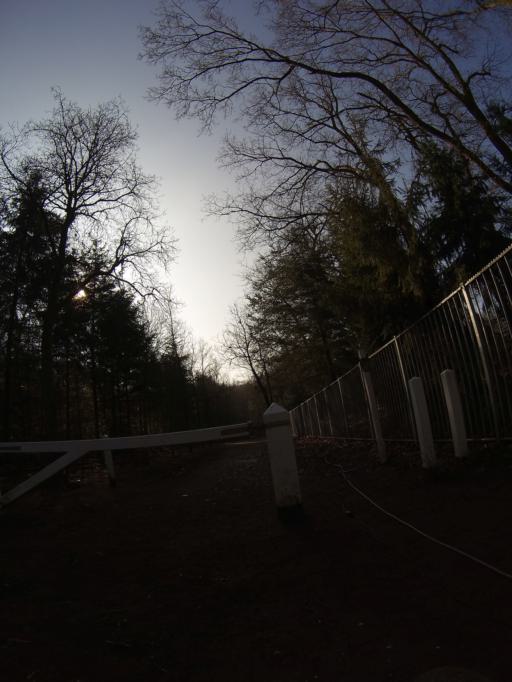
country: NL
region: Utrecht
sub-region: Gemeente Amersfoort
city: Randenbroek
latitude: 52.1383
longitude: 5.3891
